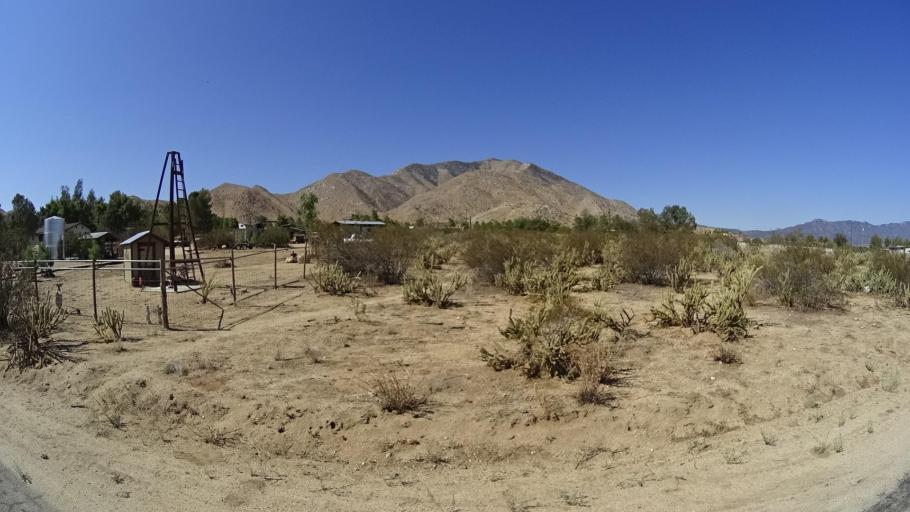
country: US
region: California
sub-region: San Diego County
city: Julian
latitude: 33.0727
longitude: -116.4364
